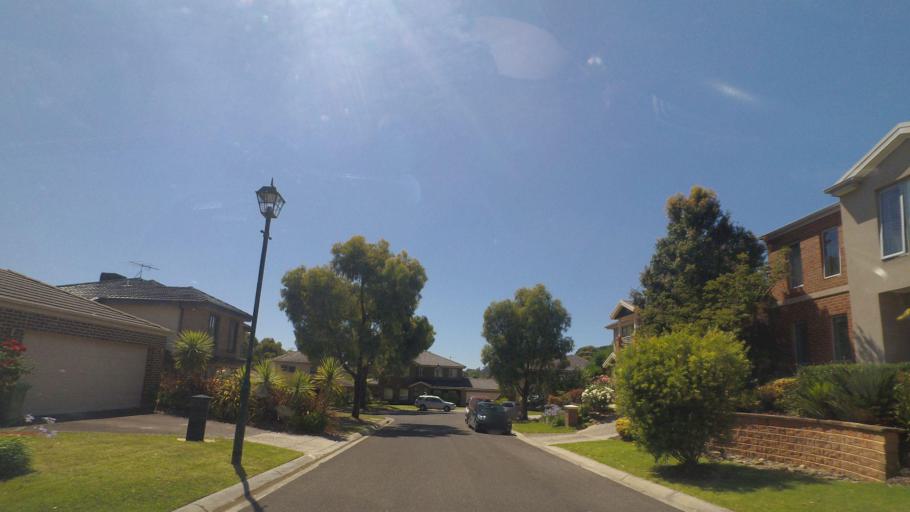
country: AU
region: Victoria
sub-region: Maroondah
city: Warranwood
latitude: -37.7819
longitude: 145.2385
